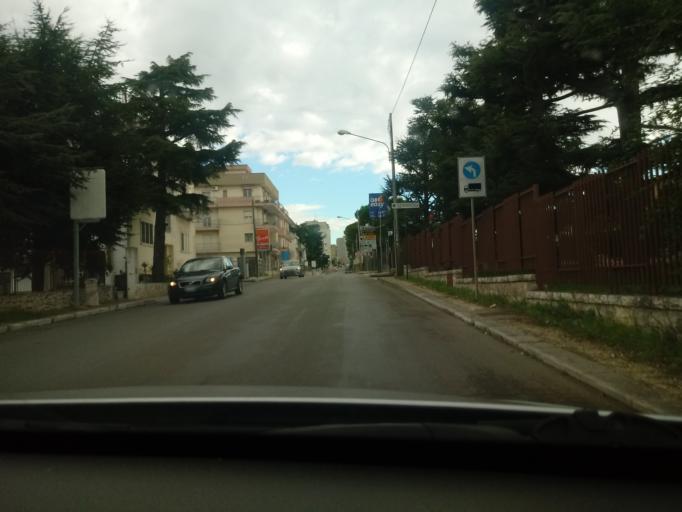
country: IT
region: Apulia
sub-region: Provincia di Bari
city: Putignano
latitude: 40.8548
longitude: 17.1141
